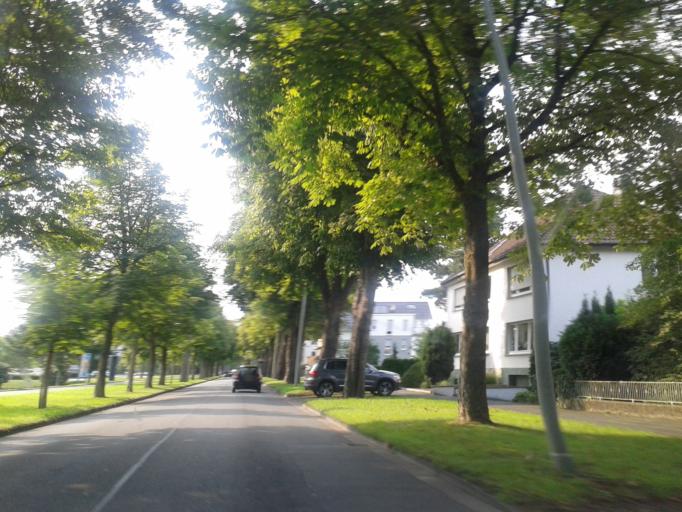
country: DE
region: North Rhine-Westphalia
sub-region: Regierungsbezirk Detmold
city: Paderborn
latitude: 51.7310
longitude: 8.7393
